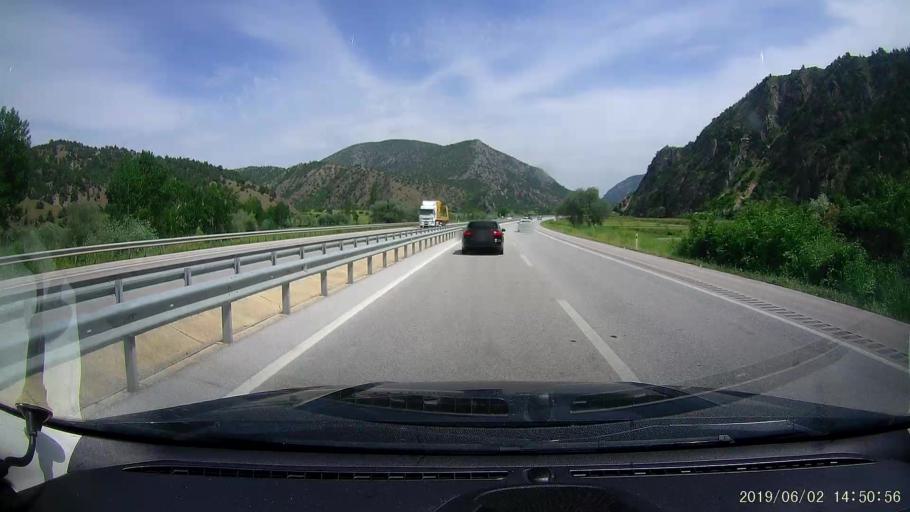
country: TR
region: Corum
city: Kargi
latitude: 41.0674
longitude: 34.5308
